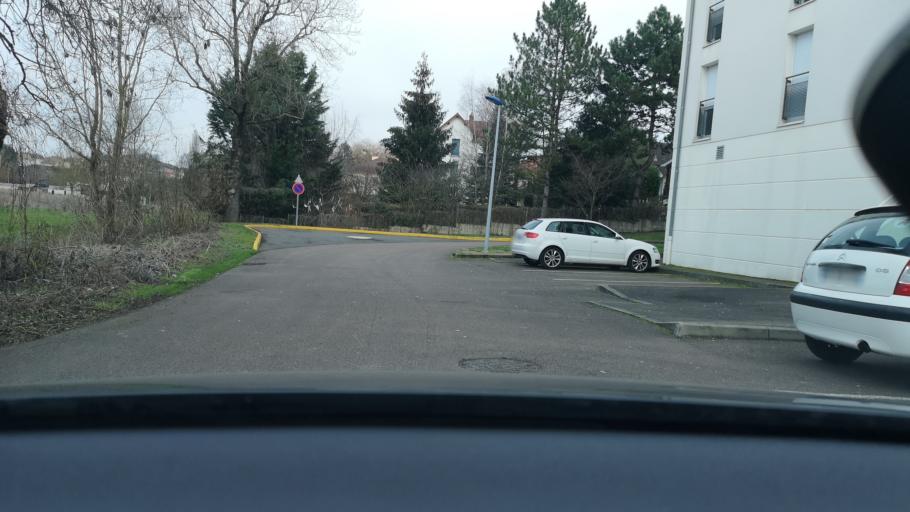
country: FR
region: Bourgogne
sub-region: Departement de Saone-et-Loire
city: Chalon-sur-Saone
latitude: 46.7814
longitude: 4.8365
